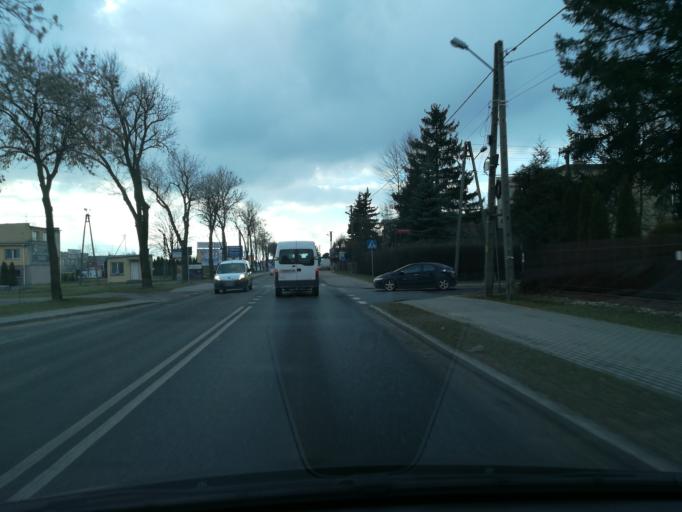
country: PL
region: Lodz Voivodeship
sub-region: Powiat radomszczanski
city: Radomsko
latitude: 51.0735
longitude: 19.4150
